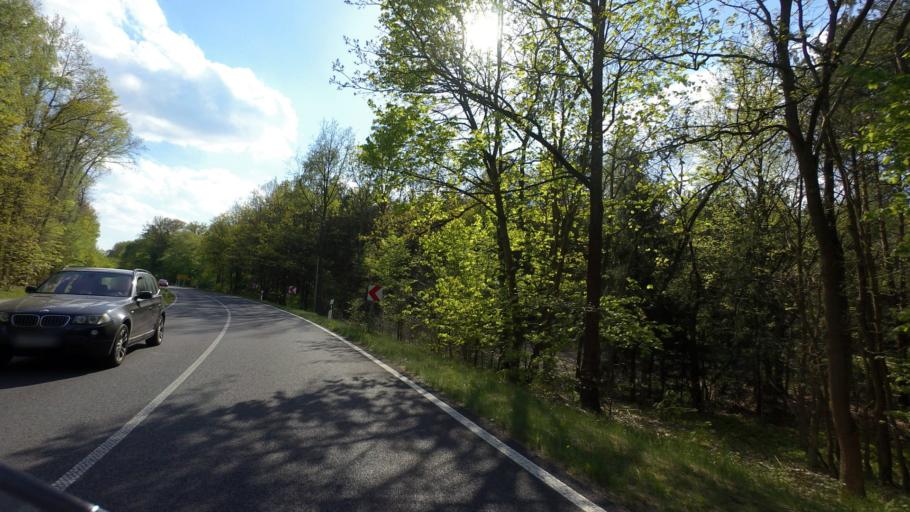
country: DE
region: Brandenburg
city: Zehdenick
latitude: 53.0061
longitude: 13.3529
